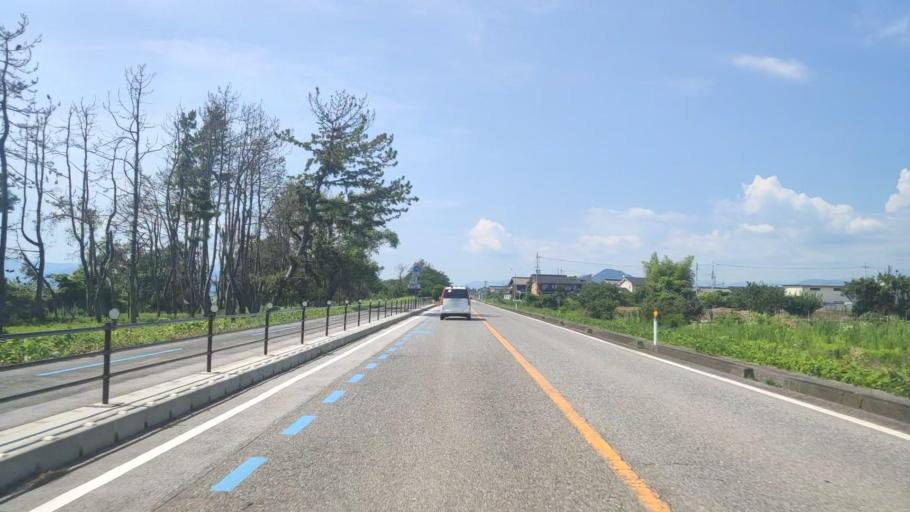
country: JP
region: Shiga Prefecture
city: Nagahama
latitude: 35.3995
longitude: 136.2170
